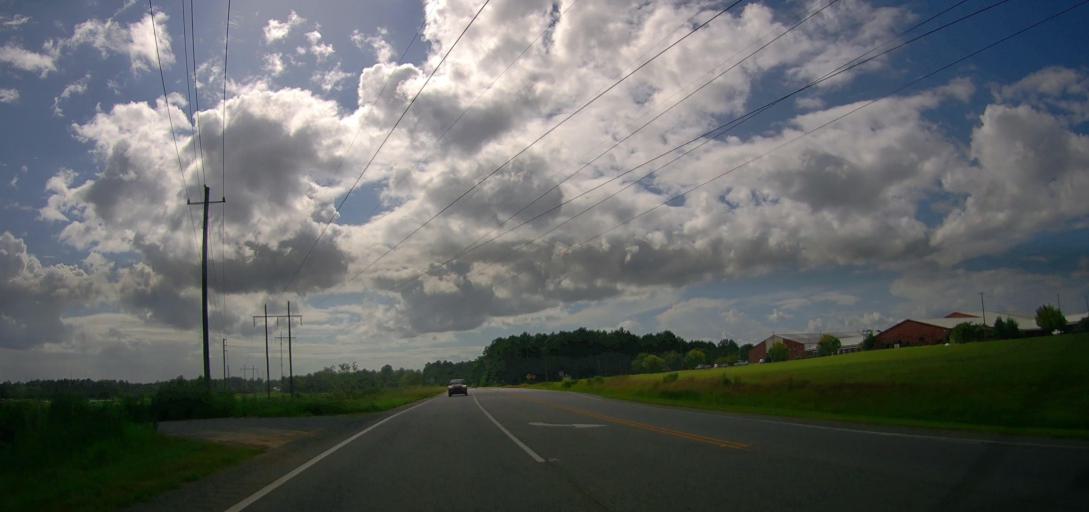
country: US
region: Georgia
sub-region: Coffee County
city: Douglas
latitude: 31.5377
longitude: -82.8341
